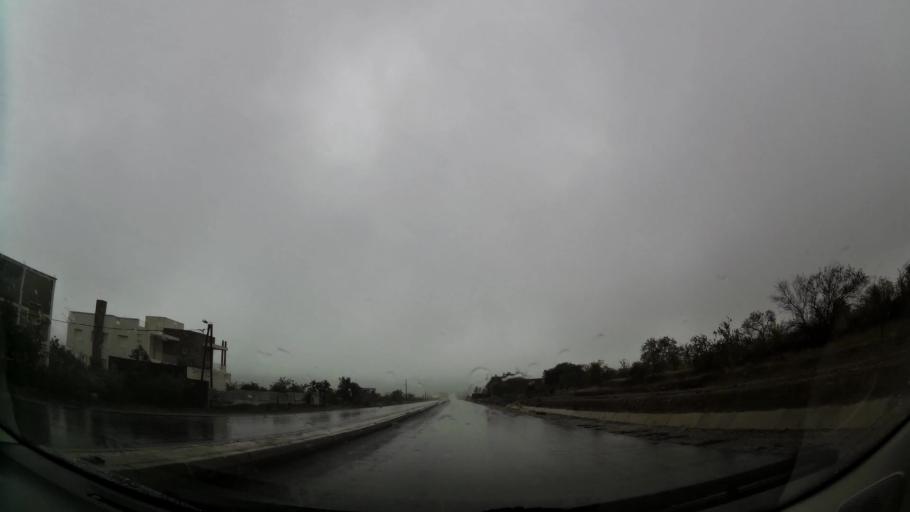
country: MA
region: Oriental
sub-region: Nador
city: Midar
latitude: 34.8470
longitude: -3.7216
